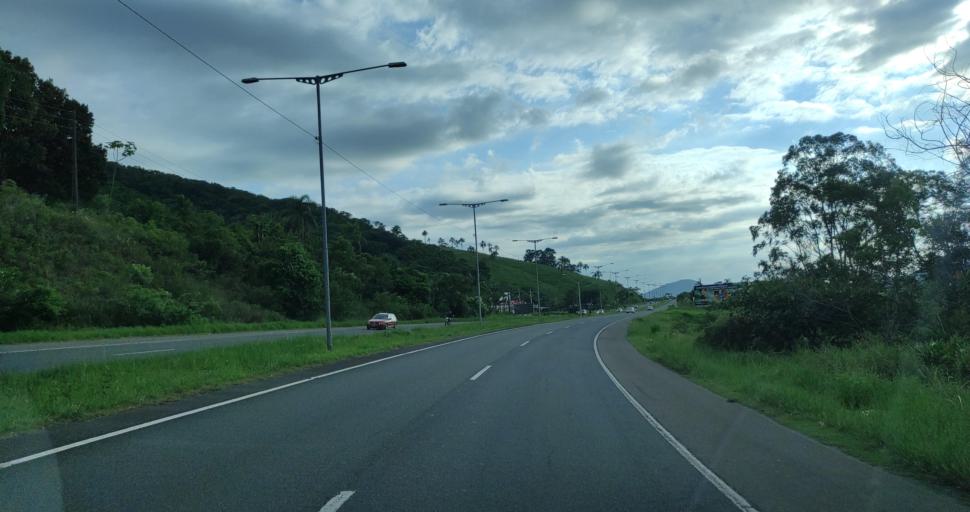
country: BR
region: Santa Catarina
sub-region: Penha
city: Penha
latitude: -26.8097
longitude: -48.6560
